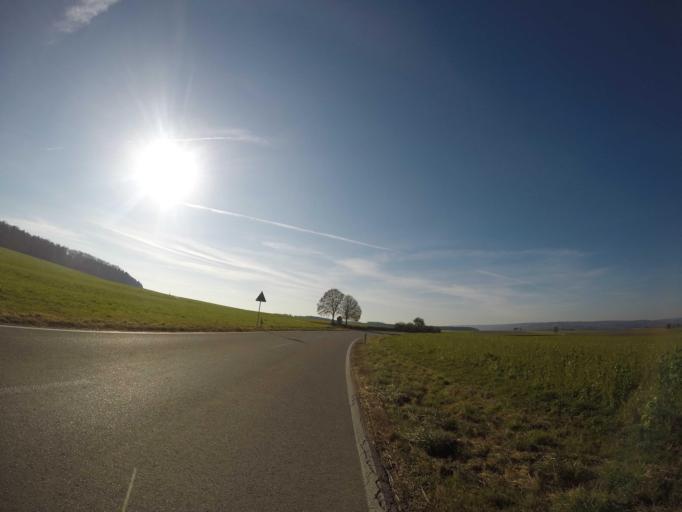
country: DE
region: Baden-Wuerttemberg
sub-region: Tuebingen Region
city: Obermarchtal
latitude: 48.2064
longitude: 9.5559
